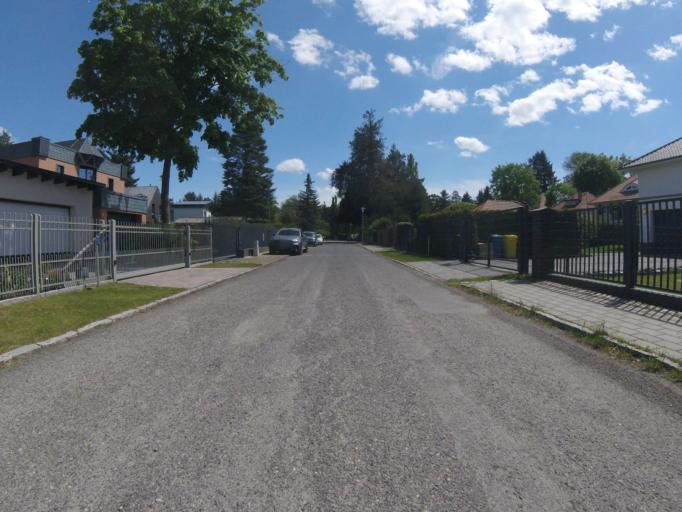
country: DE
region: Brandenburg
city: Schwerin
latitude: 52.1499
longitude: 13.6147
